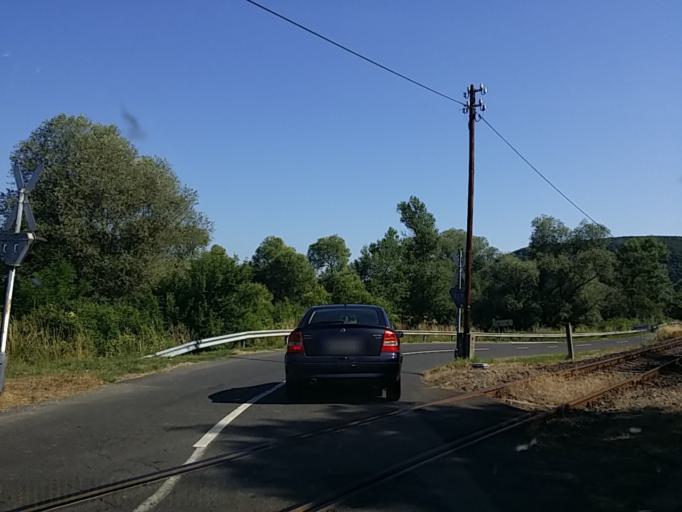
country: HU
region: Nograd
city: Szecseny
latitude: 48.1877
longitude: 19.5271
